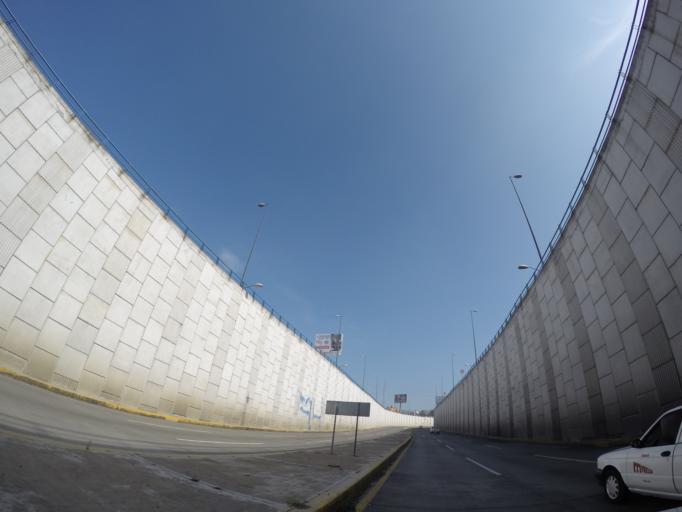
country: MX
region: Michoacan
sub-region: Morelia
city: San Antonio
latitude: 19.7014
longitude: -101.2439
